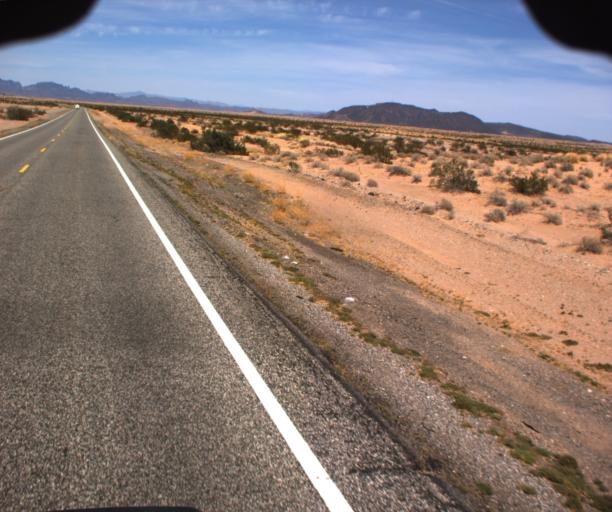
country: US
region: Arizona
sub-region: La Paz County
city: Parker
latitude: 34.0571
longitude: -114.2577
